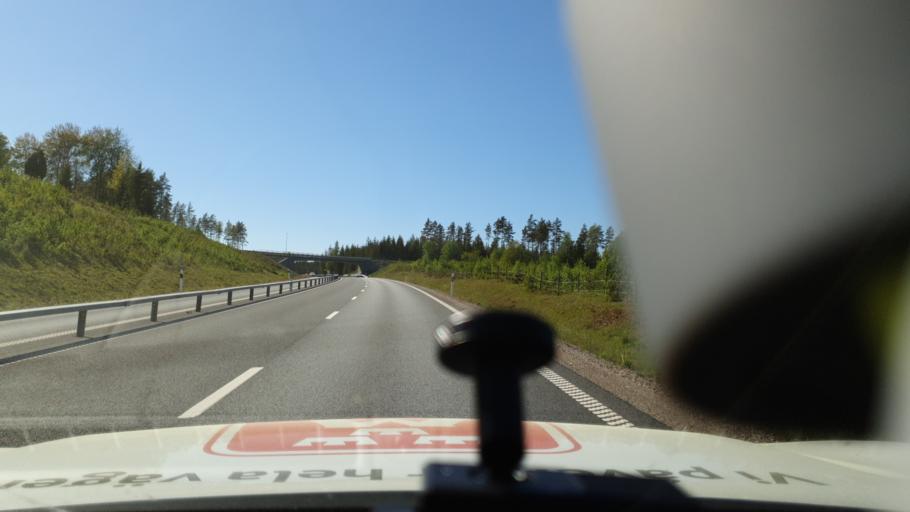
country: SE
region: Joenkoeping
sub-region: Vetlanda Kommun
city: Vetlanda
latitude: 57.4212
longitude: 15.1994
